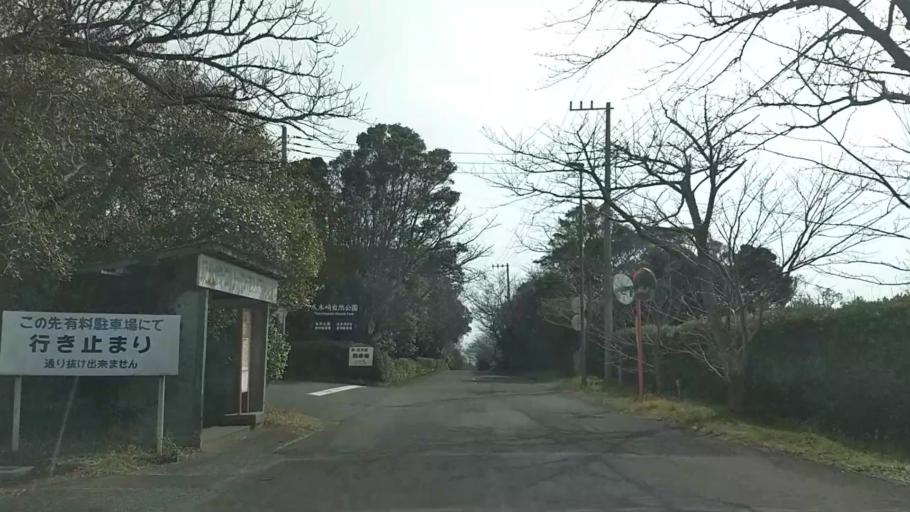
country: JP
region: Shizuoka
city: Shimoda
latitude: 34.6643
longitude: 138.9801
